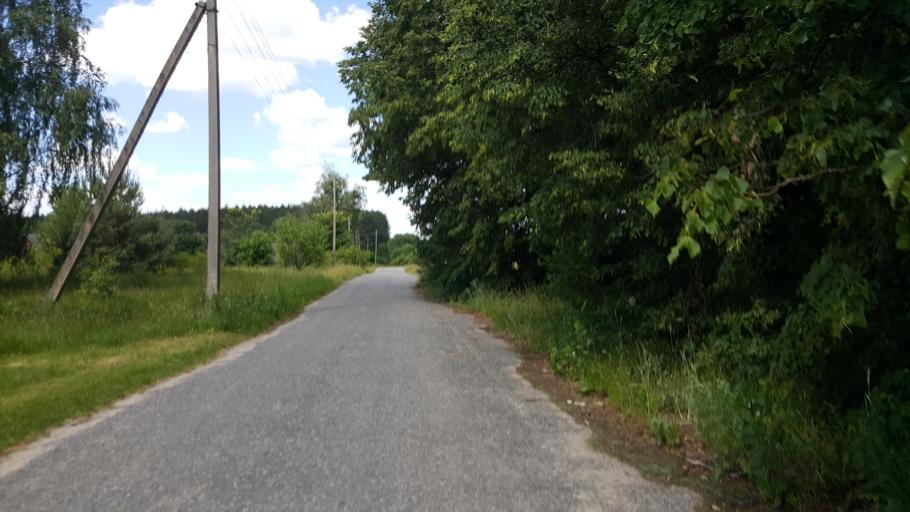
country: PL
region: Podlasie
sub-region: Powiat hajnowski
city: Czeremcha
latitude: 52.5112
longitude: 23.5476
